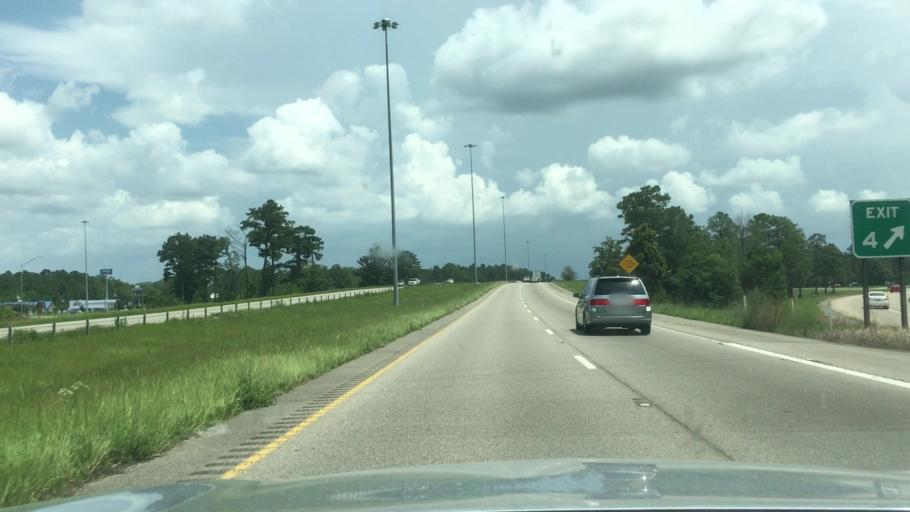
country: US
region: Mississippi
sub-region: Pearl River County
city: Picayune
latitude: 30.5146
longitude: -89.6645
